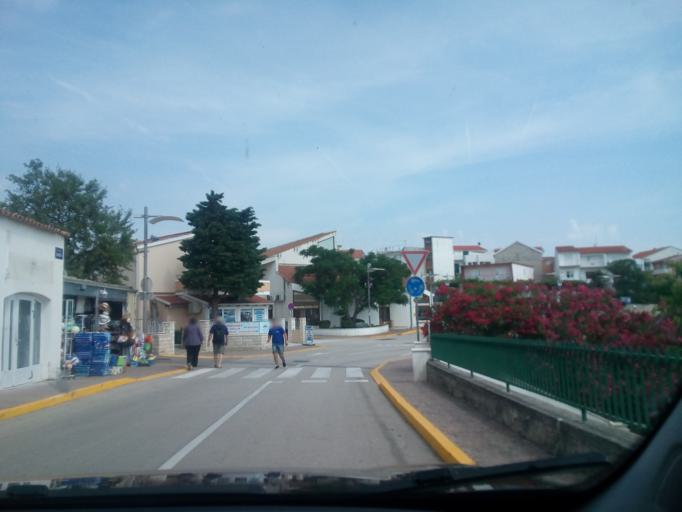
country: HR
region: Sibensko-Kniniska
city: Primosten
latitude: 43.5886
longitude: 15.9243
